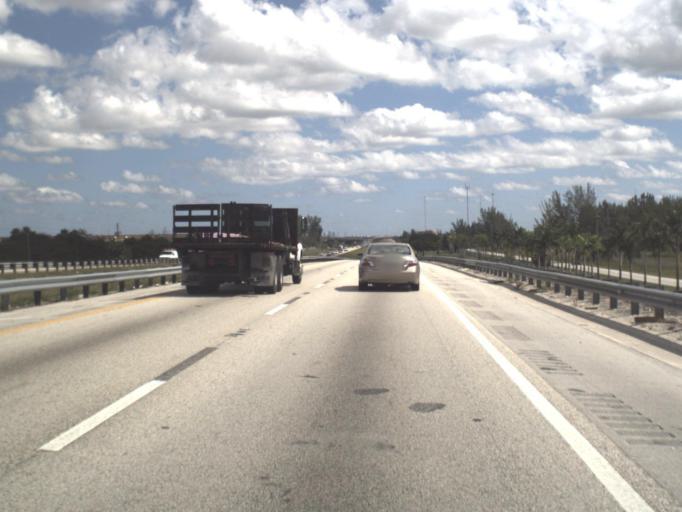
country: US
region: Florida
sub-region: Miami-Dade County
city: Lake Lucerne
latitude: 25.9713
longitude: -80.2781
